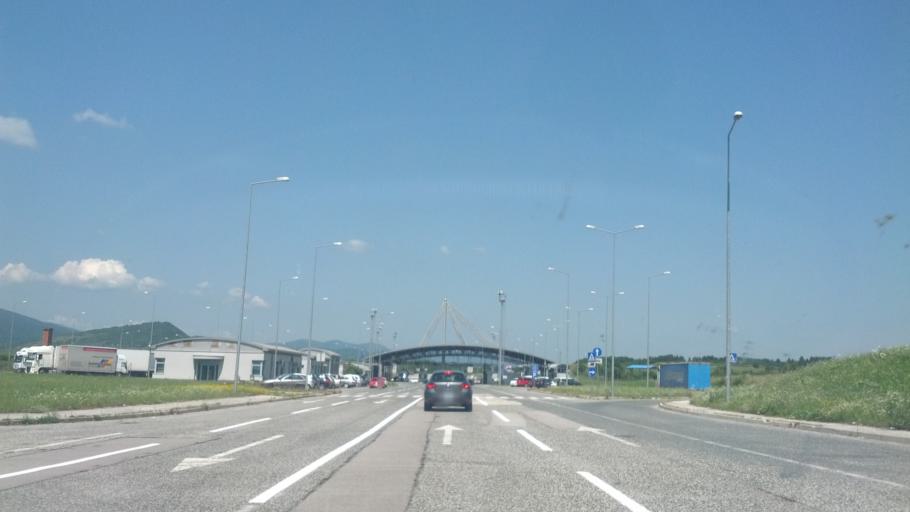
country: BA
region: Federation of Bosnia and Herzegovina
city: Izacic
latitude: 44.8733
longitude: 15.7669
